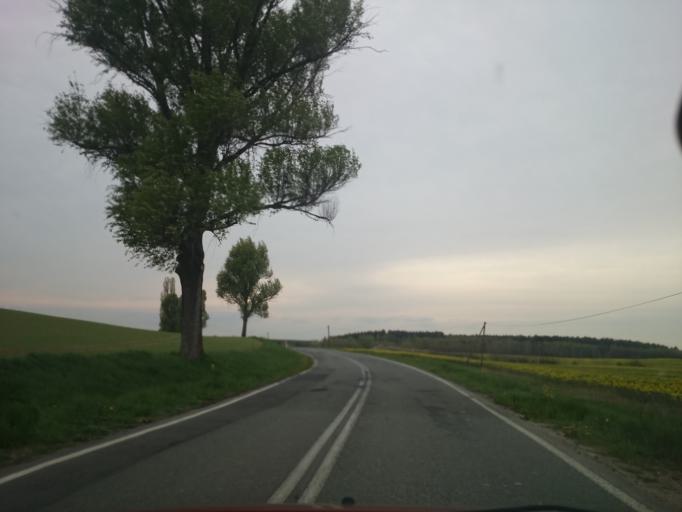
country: PL
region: Lower Silesian Voivodeship
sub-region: Powiat strzelinski
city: Przeworno
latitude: 50.6454
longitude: 17.2069
